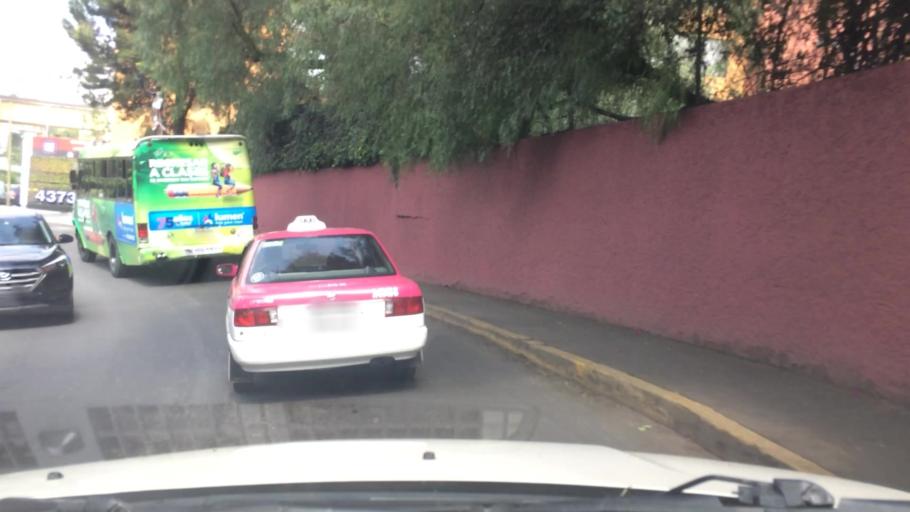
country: MX
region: Mexico City
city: Magdalena Contreras
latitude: 19.3461
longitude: -99.2109
